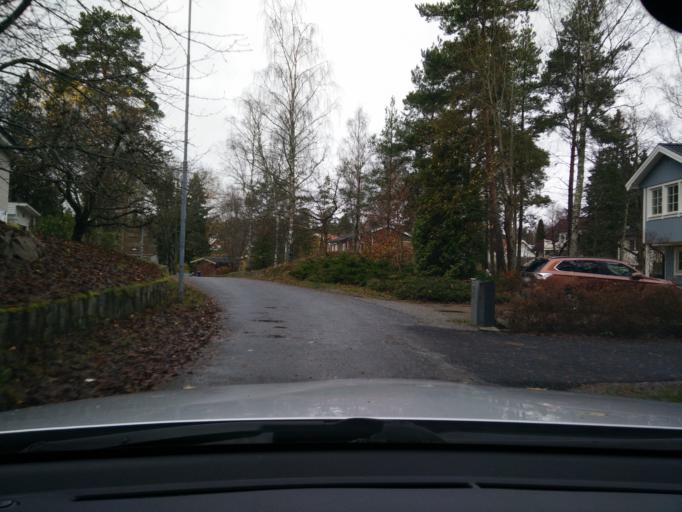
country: SE
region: Stockholm
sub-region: Sollentuna Kommun
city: Sollentuna
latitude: 59.4619
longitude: 17.9504
